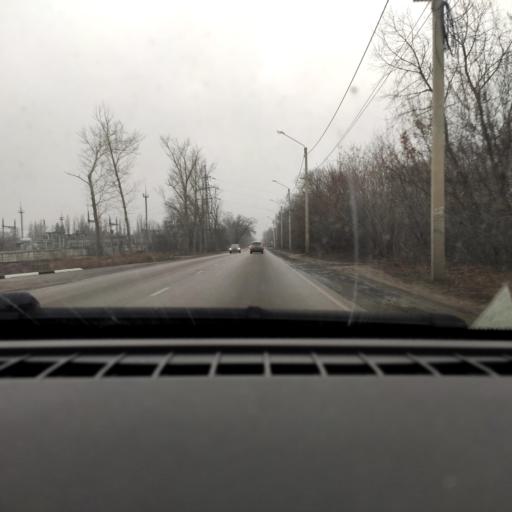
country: RU
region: Voronezj
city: Maslovka
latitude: 51.5844
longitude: 39.1666
